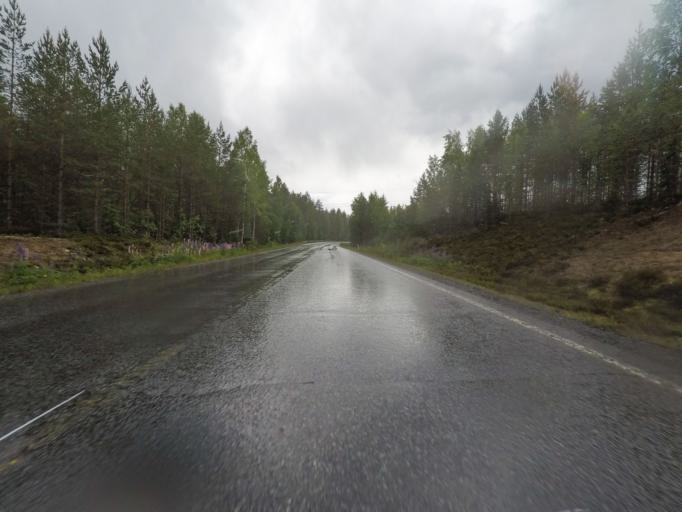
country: FI
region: Central Finland
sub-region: Jyvaeskylae
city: Toivakka
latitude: 62.1795
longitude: 26.1794
